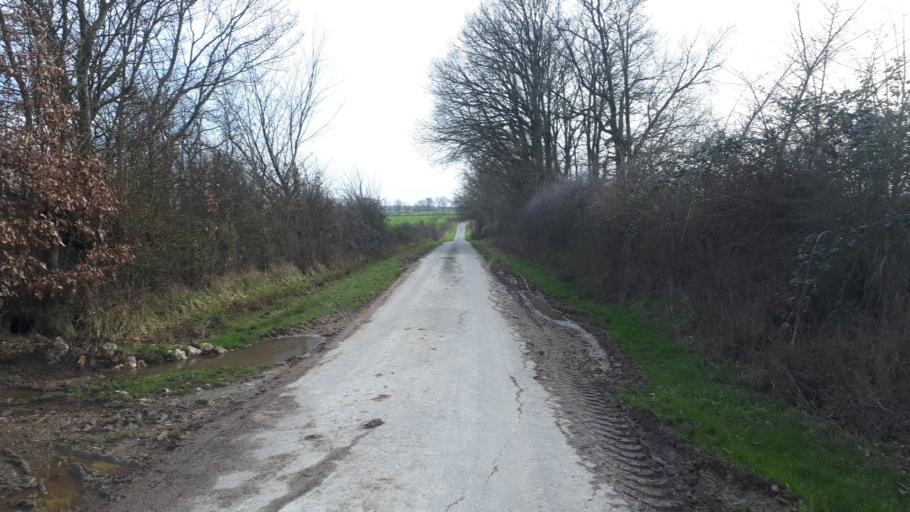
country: FR
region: Poitou-Charentes
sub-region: Departement de la Vienne
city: Archigny
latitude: 46.6252
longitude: 0.7456
